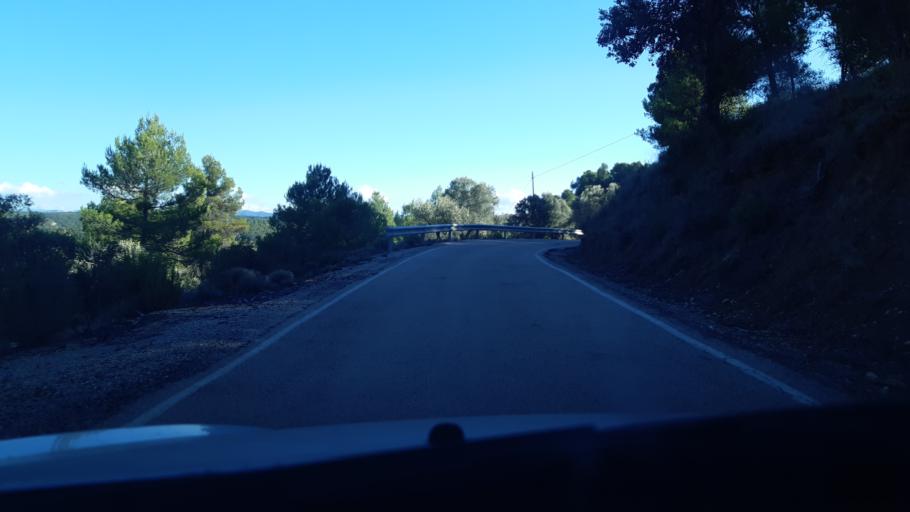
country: ES
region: Aragon
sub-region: Provincia de Teruel
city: Fornoles
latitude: 40.9081
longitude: -0.0136
